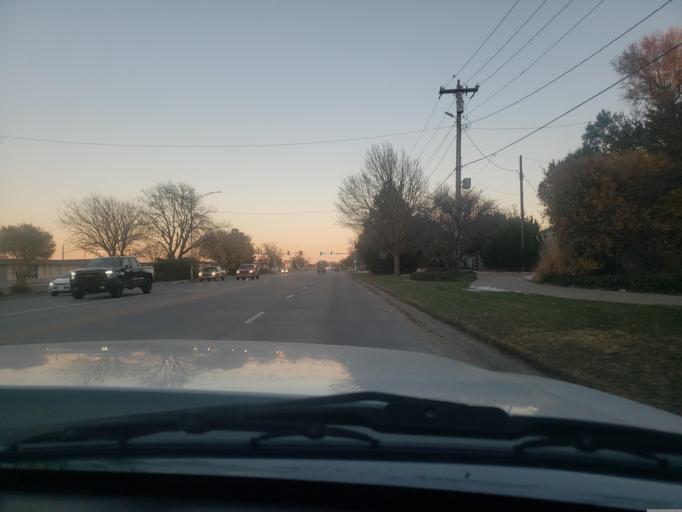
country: US
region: Kansas
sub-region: Finney County
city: Garden City
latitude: 37.9750
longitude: -100.8606
